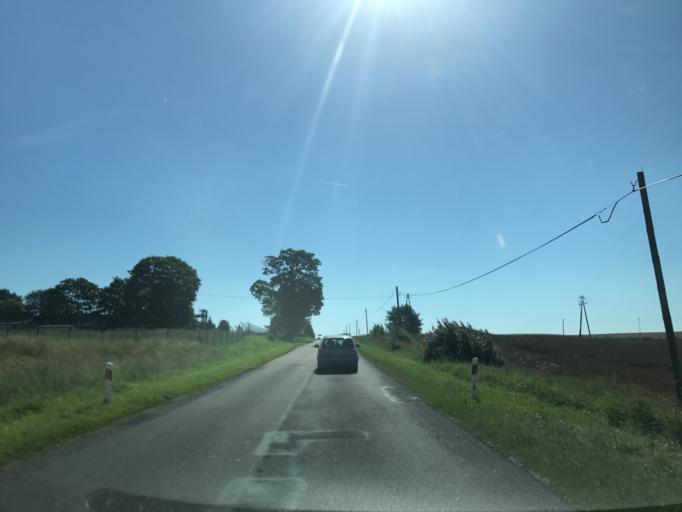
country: PL
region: Pomeranian Voivodeship
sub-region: Powiat bytowski
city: Czarna Dabrowka
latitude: 54.3656
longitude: 17.5090
